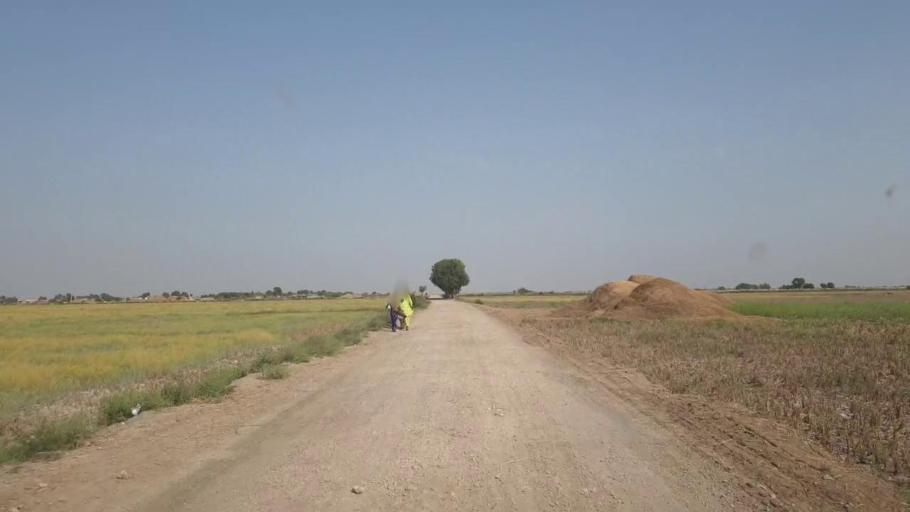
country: PK
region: Sindh
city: Kario
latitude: 24.5356
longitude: 68.5411
